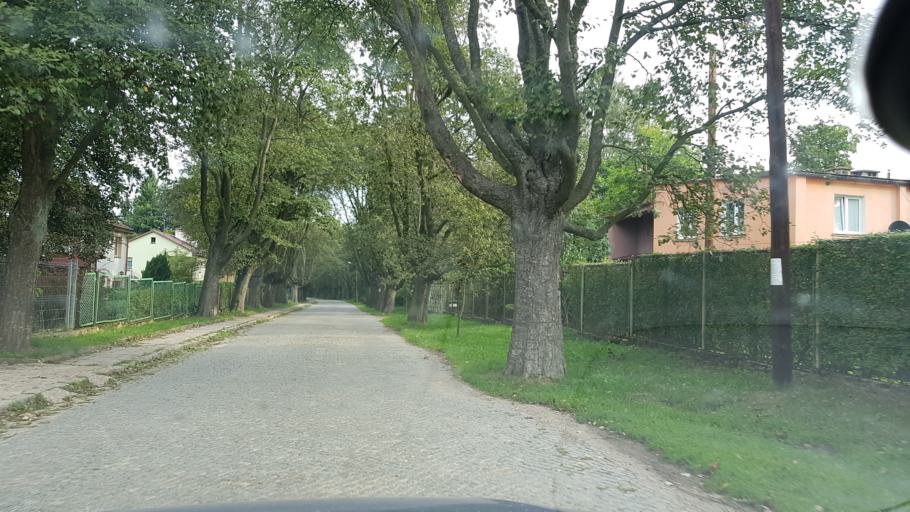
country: PL
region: Lower Silesian Voivodeship
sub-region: Powiat jeleniogorski
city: Janowice Wielkie
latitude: 50.8755
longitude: 15.9197
